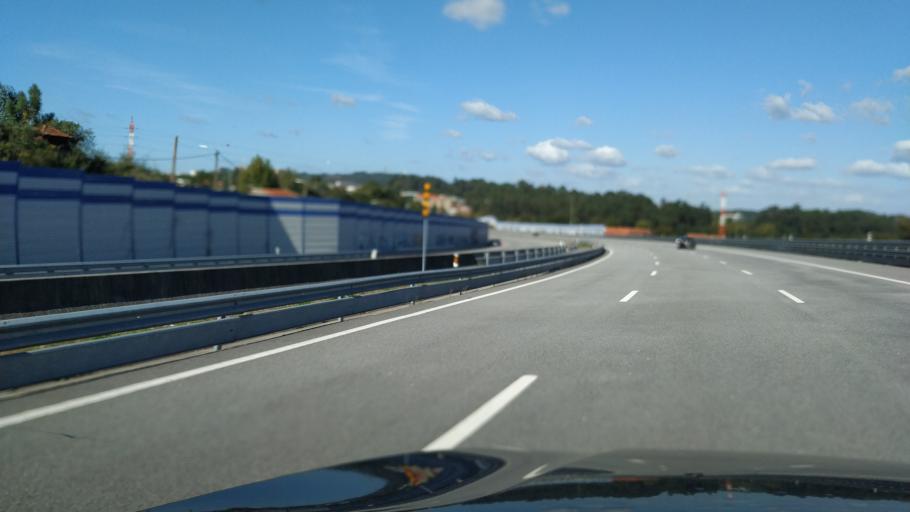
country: PT
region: Porto
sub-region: Vila Nova de Gaia
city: Avintes
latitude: 41.0852
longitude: -8.5523
